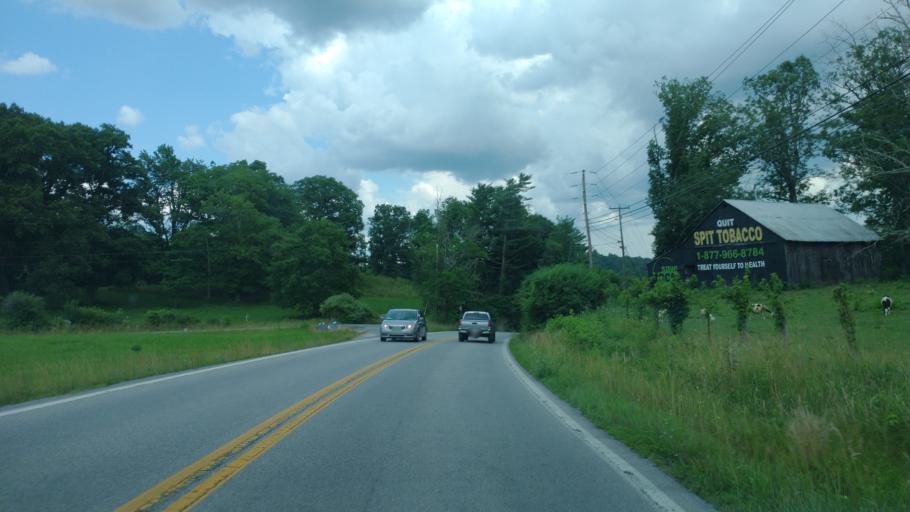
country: US
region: West Virginia
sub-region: Mercer County
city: Athens
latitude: 37.4480
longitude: -81.0027
